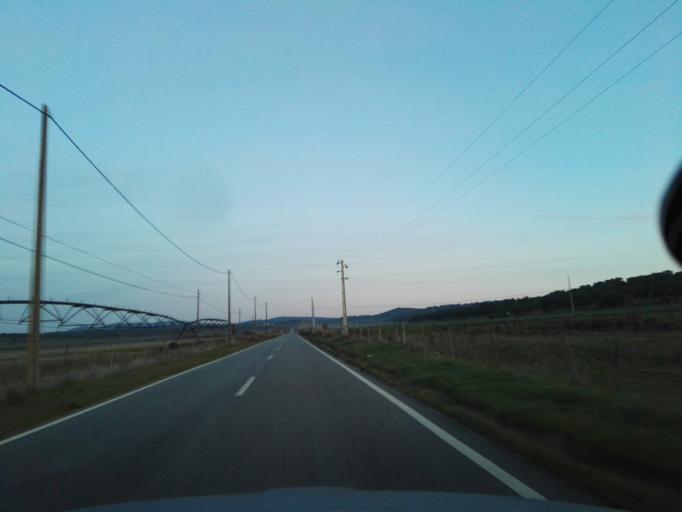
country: PT
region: Evora
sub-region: Arraiolos
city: Arraiolos
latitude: 38.7619
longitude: -8.1155
